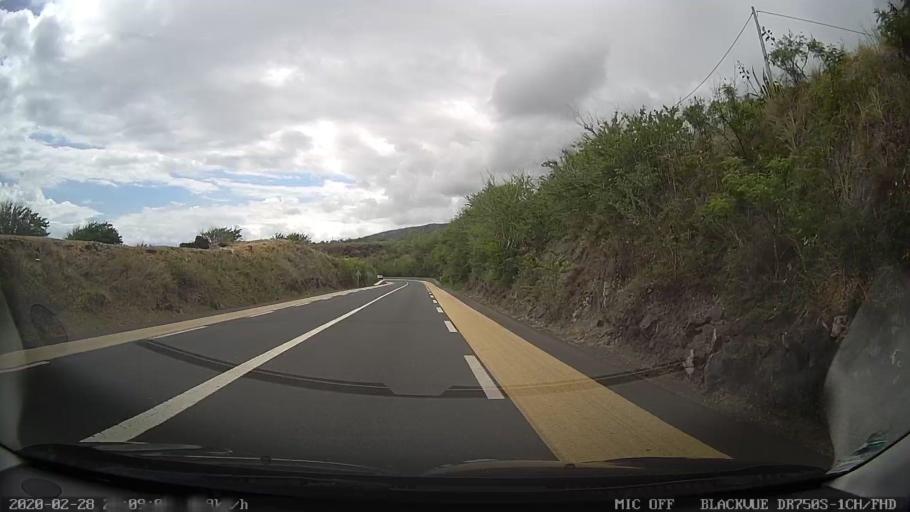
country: RE
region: Reunion
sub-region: Reunion
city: Trois-Bassins
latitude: -21.1283
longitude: 55.2693
